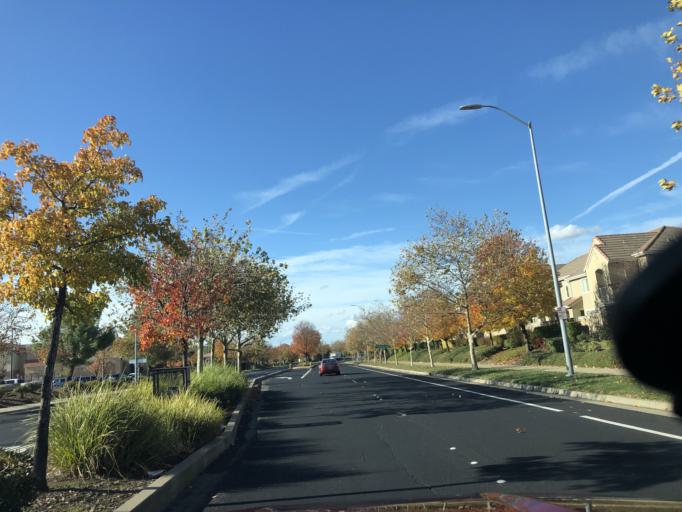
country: US
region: California
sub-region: Placer County
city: Roseville
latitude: 38.7911
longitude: -121.2877
